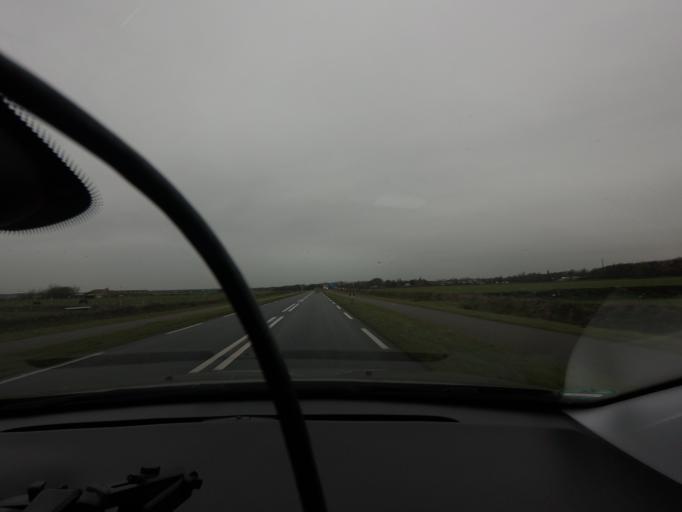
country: NL
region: North Holland
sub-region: Gemeente Texel
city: Den Burg
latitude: 53.0451
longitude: 4.7960
